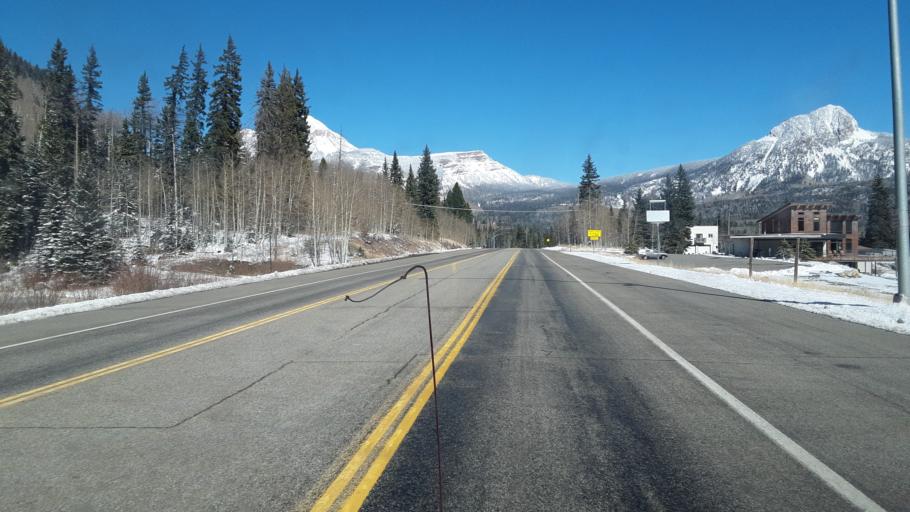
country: US
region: Colorado
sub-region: San Juan County
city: Silverton
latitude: 37.6317
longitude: -107.8084
